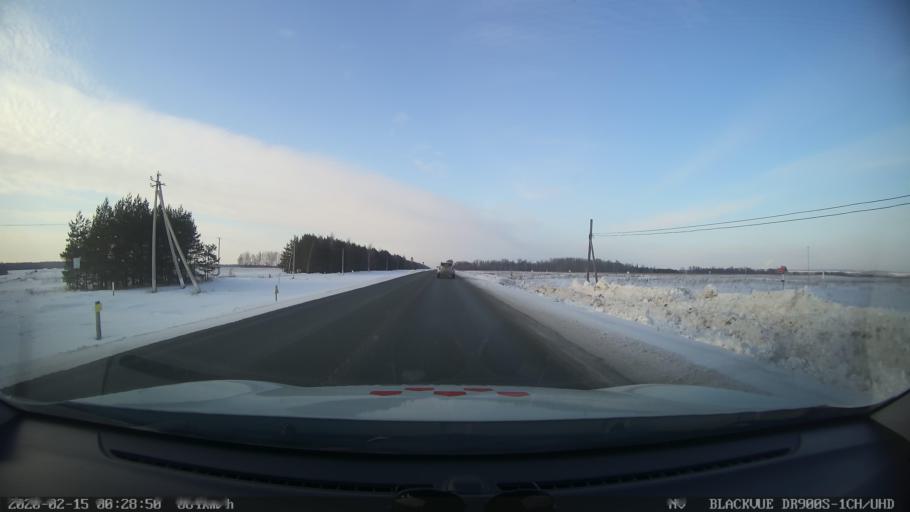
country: RU
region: Tatarstan
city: Verkhniy Uslon
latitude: 55.6457
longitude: 48.8735
